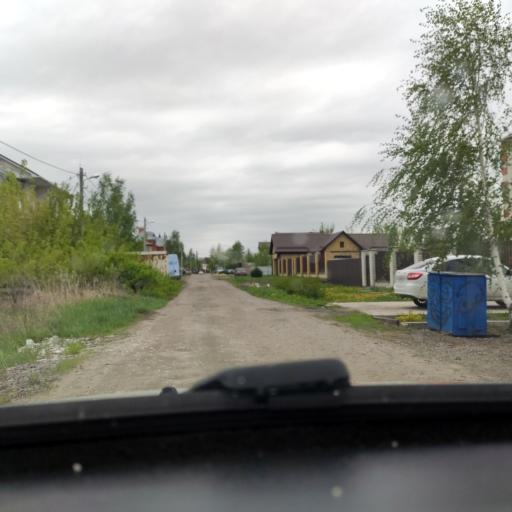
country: RU
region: Voronezj
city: Somovo
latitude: 51.6852
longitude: 39.3101
